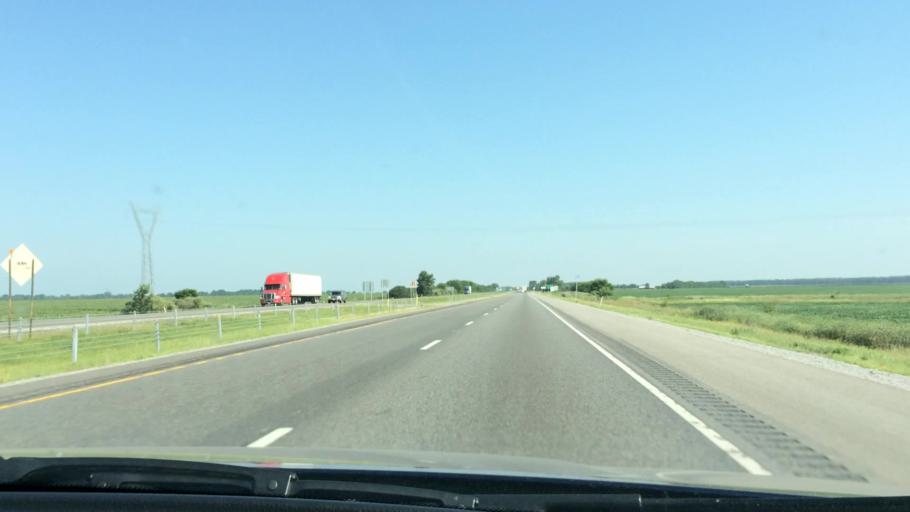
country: US
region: Indiana
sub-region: Jasper County
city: Remington
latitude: 40.7718
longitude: -87.1233
